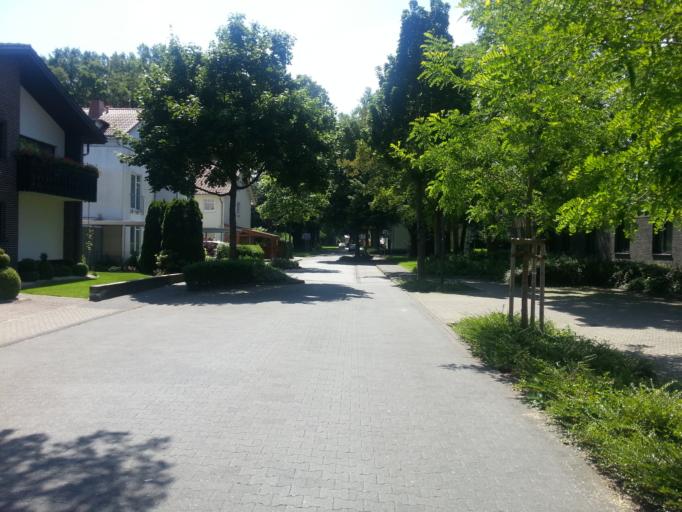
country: DE
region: North Rhine-Westphalia
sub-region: Regierungsbezirk Detmold
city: Paderborn
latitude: 51.7397
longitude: 8.6843
